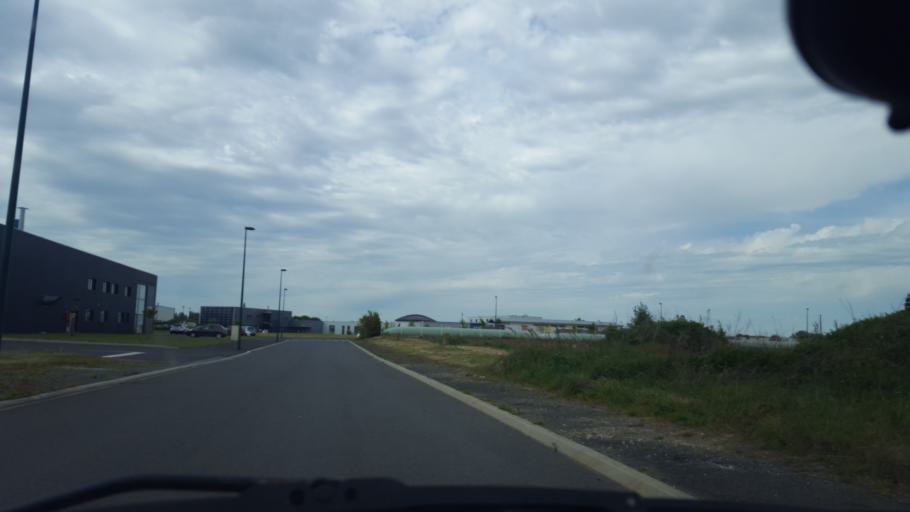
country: FR
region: Pays de la Loire
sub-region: Departement de la Loire-Atlantique
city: Machecoul
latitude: 46.9766
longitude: -1.8016
